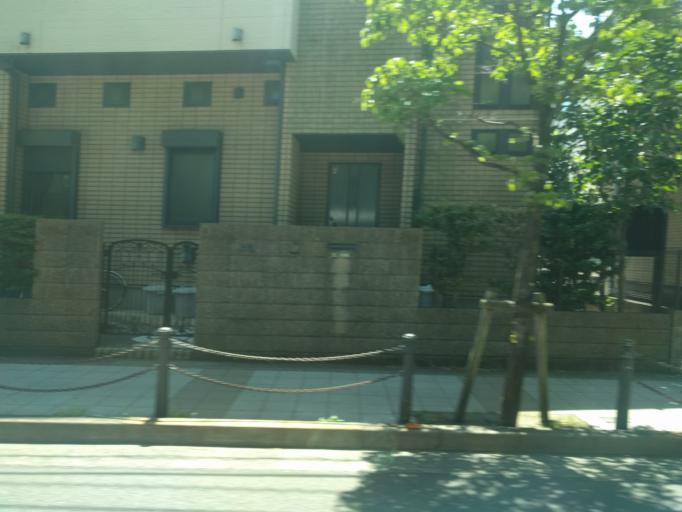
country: JP
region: Tokyo
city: Mitaka-shi
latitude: 35.6651
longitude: 139.6191
